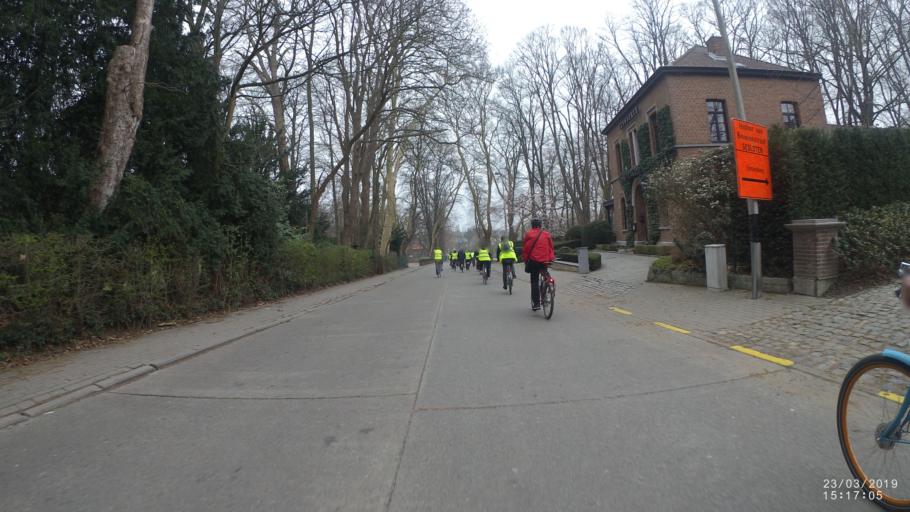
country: BE
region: Flanders
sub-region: Provincie Vlaams-Brabant
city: Dilbeek
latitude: 50.8723
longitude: 4.2653
